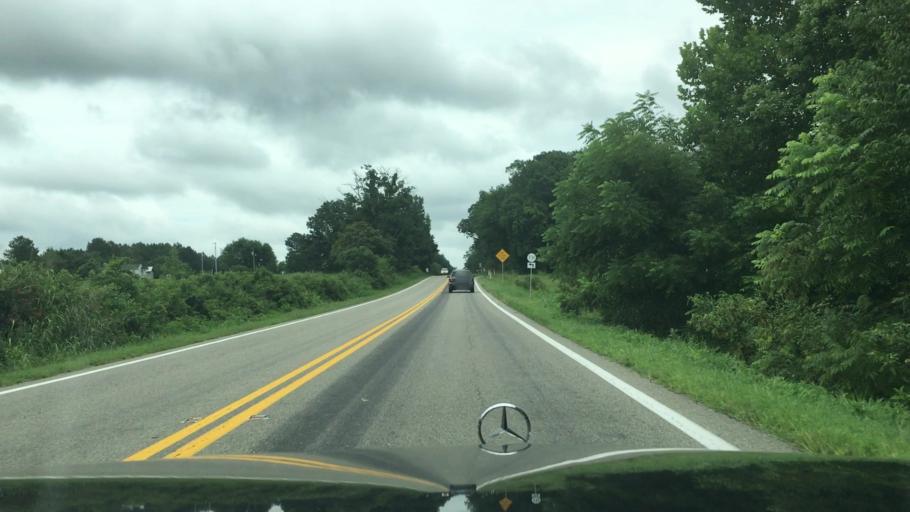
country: US
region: Virginia
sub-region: Prince Edward County
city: Farmville
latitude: 37.2740
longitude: -78.2563
